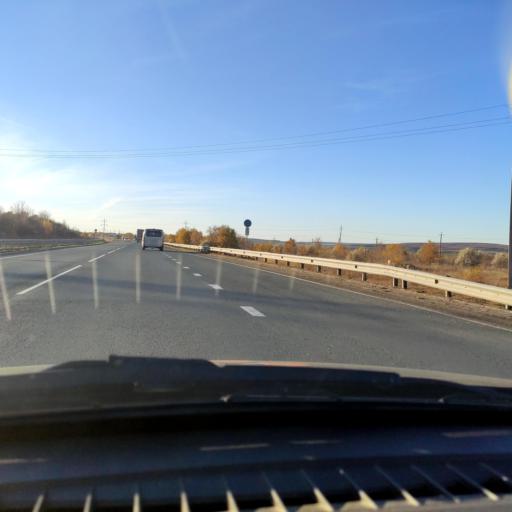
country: RU
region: Samara
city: Varlamovo
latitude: 53.1929
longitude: 48.3352
